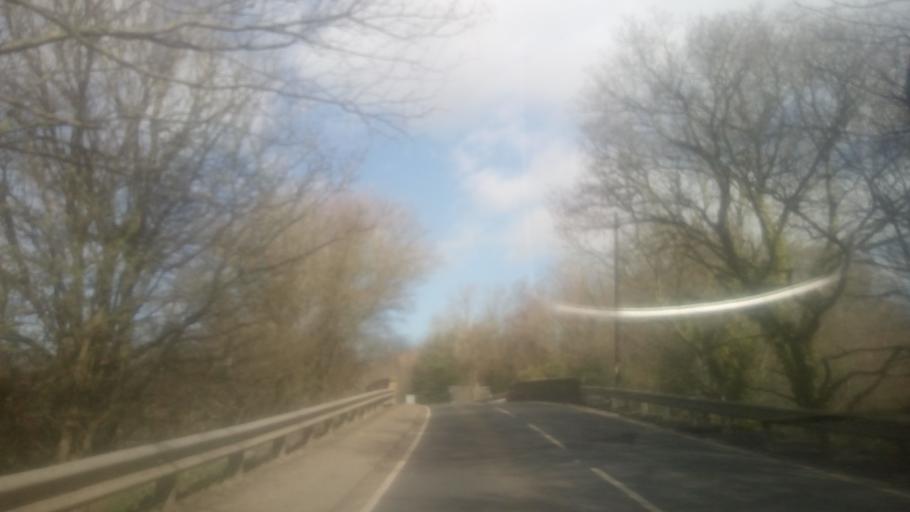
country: GB
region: Scotland
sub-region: East Lothian
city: Ormiston
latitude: 55.9166
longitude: -2.9349
